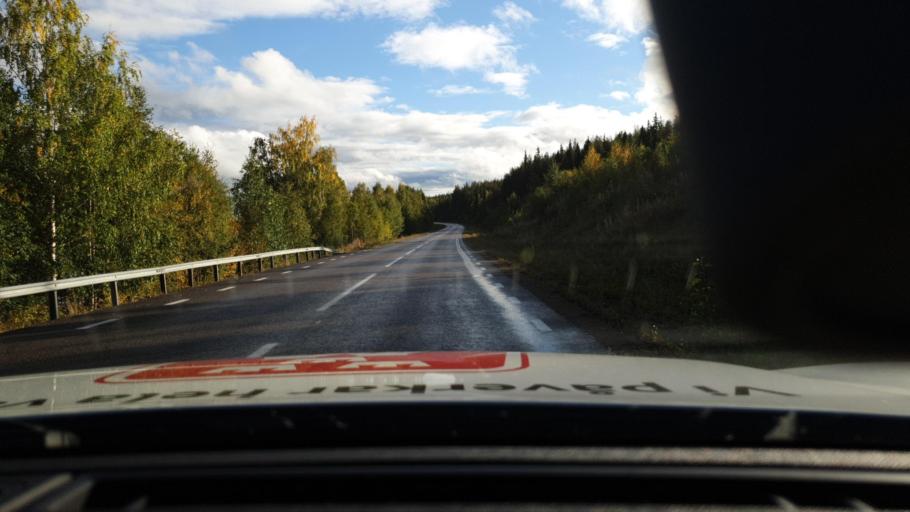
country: SE
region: Norrbotten
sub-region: Overkalix Kommun
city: OEverkalix
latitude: 66.7499
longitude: 22.6719
